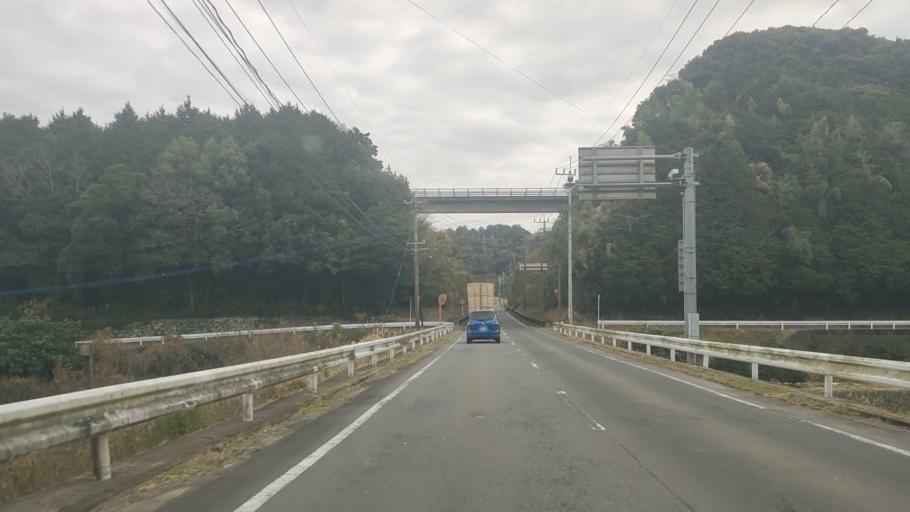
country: JP
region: Nagasaki
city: Shimabara
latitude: 32.8489
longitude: 130.2326
